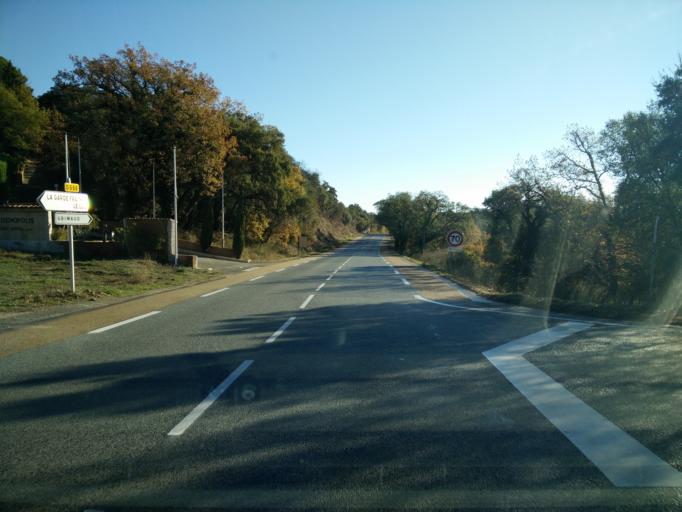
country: FR
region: Provence-Alpes-Cote d'Azur
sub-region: Departement du Var
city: Grimaud
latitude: 43.2882
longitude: 6.4981
